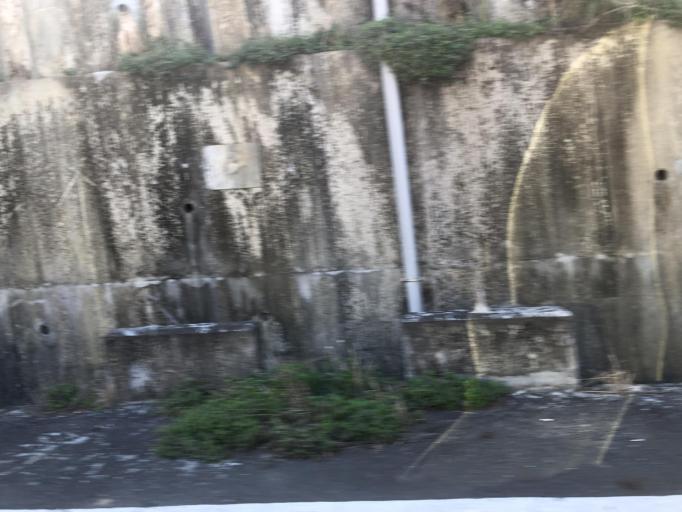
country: TW
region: Taiwan
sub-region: Tainan
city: Tainan
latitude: 23.0355
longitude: 120.3432
